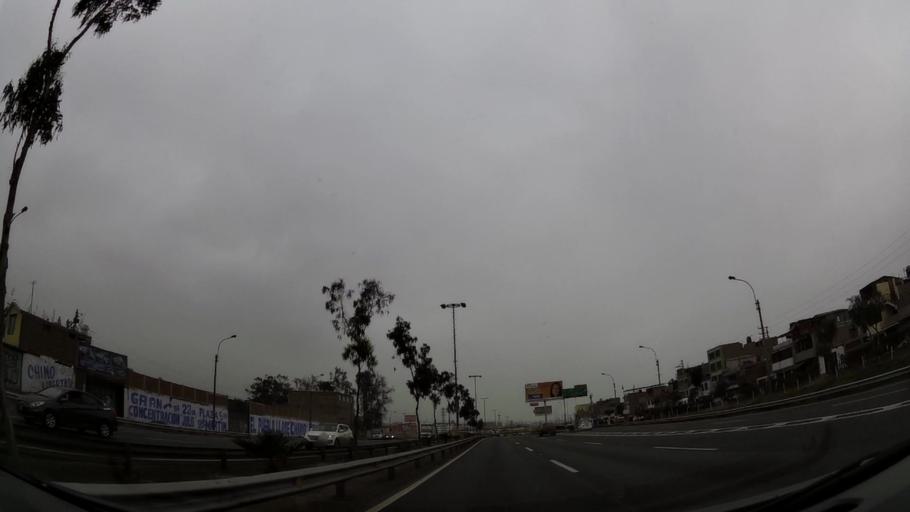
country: PE
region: Lima
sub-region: Lima
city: Surco
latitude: -12.1889
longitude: -76.9735
